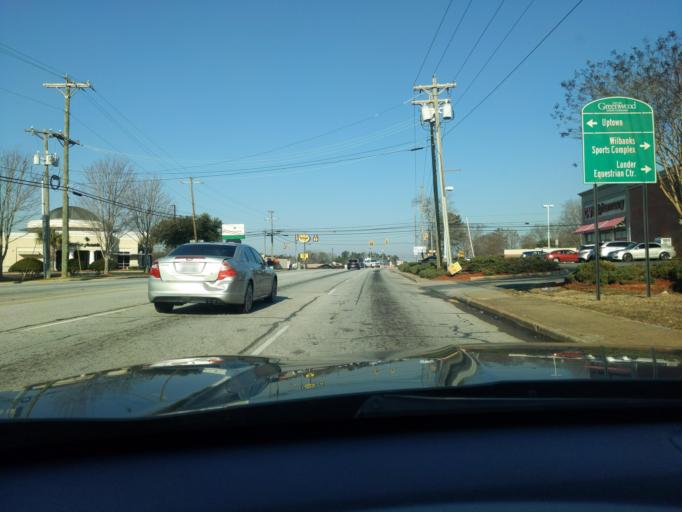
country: US
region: South Carolina
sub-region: Greenwood County
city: Greenwood
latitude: 34.2082
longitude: -82.1452
